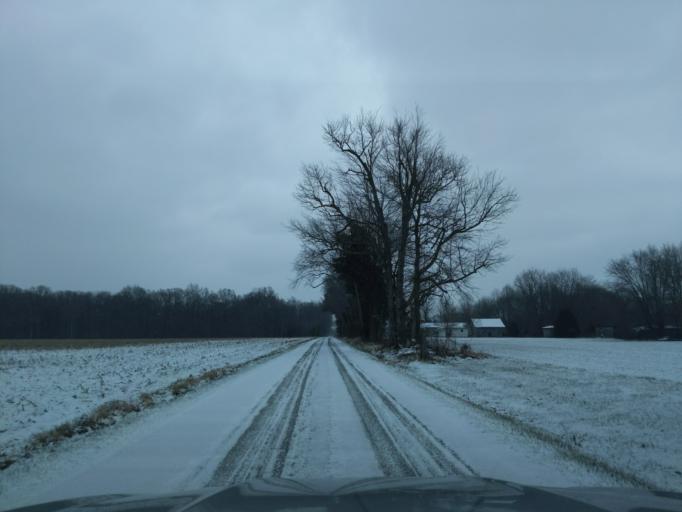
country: US
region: Indiana
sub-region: Decatur County
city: Westport
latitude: 39.2048
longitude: -85.5071
